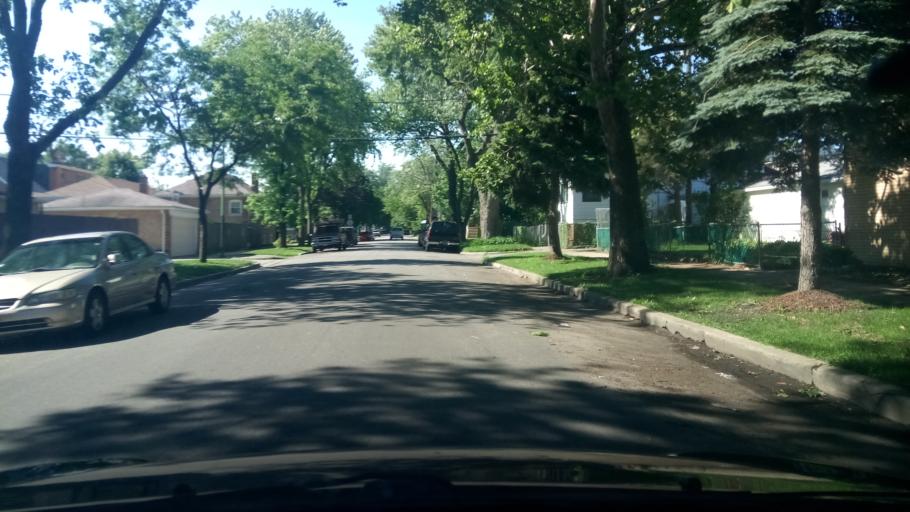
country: US
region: Illinois
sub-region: Cook County
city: Hometown
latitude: 41.7763
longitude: -87.7202
